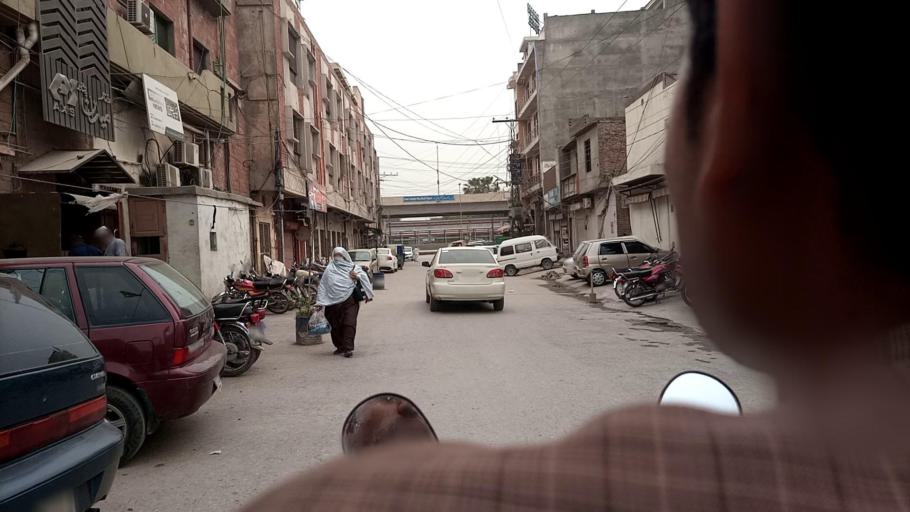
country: PK
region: Khyber Pakhtunkhwa
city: Peshawar
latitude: 34.0166
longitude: 71.5917
